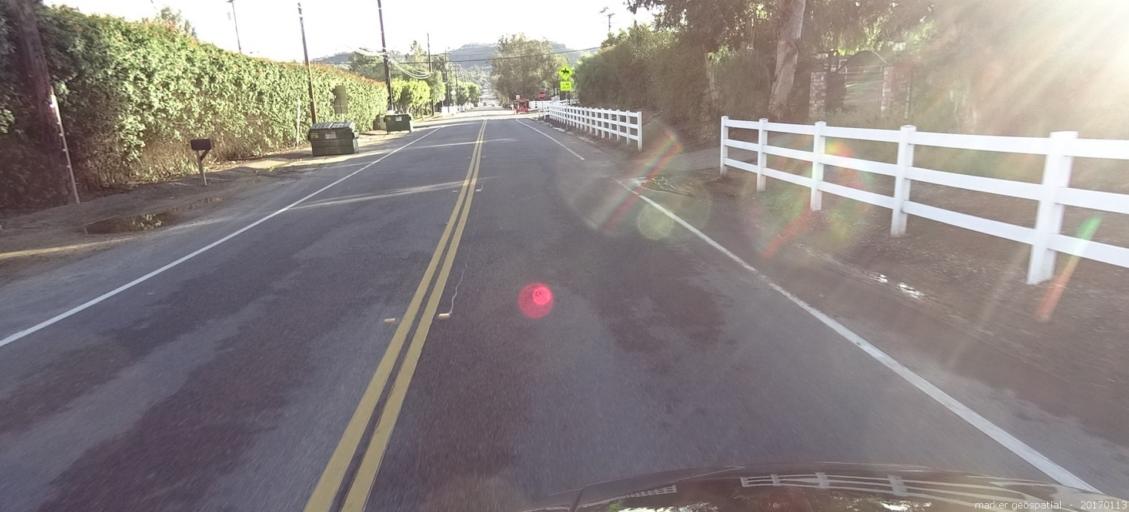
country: US
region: California
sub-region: Orange County
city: Villa Park
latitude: 33.8059
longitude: -117.7825
